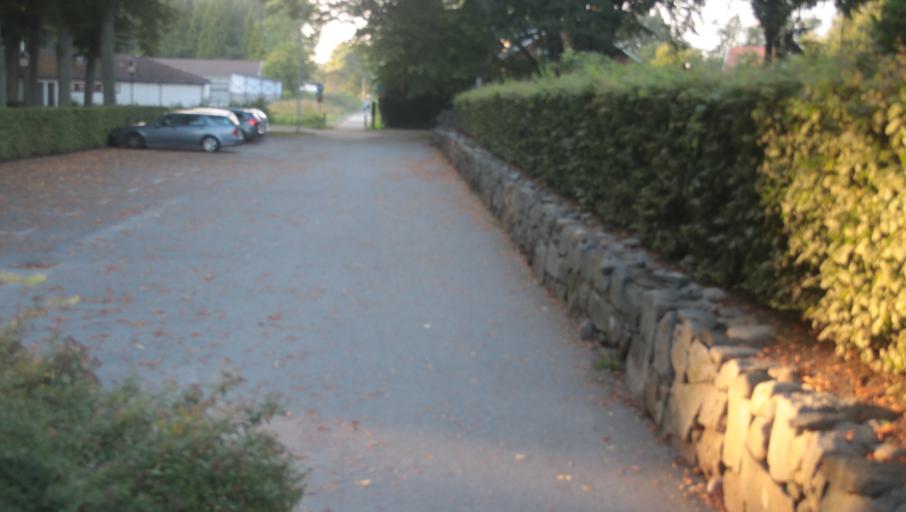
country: SE
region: Blekinge
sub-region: Karlshamns Kommun
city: Karlshamn
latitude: 56.2058
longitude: 14.8324
